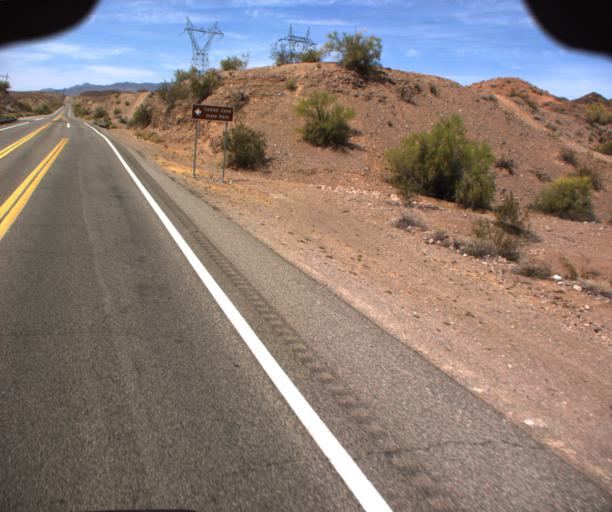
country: US
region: Arizona
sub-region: La Paz County
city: Cienega Springs
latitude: 34.3599
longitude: -114.1575
